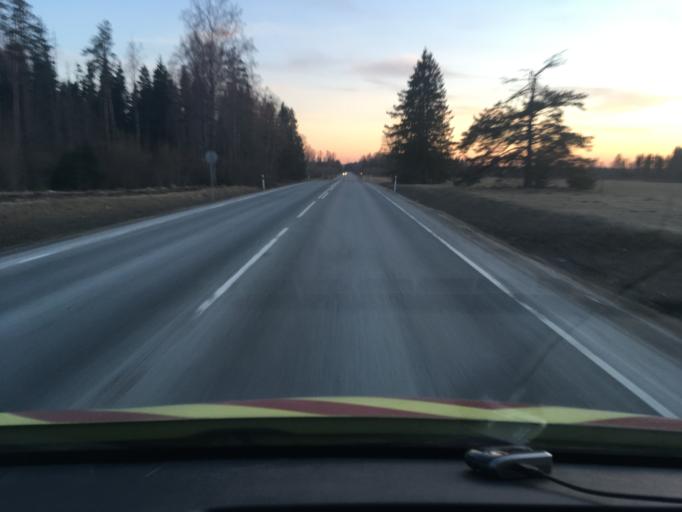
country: EE
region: Raplamaa
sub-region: Rapla vald
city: Rapla
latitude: 59.0355
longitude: 24.8297
